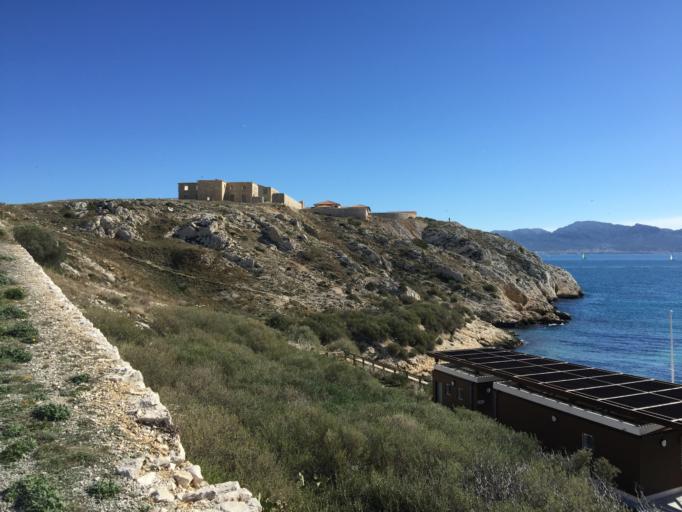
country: FR
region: Provence-Alpes-Cote d'Azur
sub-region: Departement des Bouches-du-Rhone
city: Marseille 07
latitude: 43.2847
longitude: 5.3160
